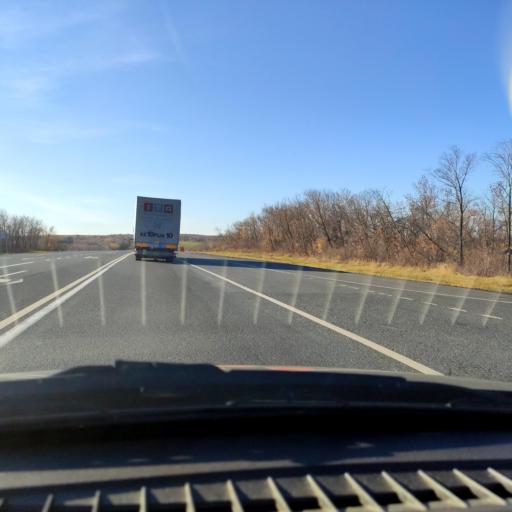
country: RU
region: Samara
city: Mezhdurechensk
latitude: 53.2565
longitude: 49.1287
